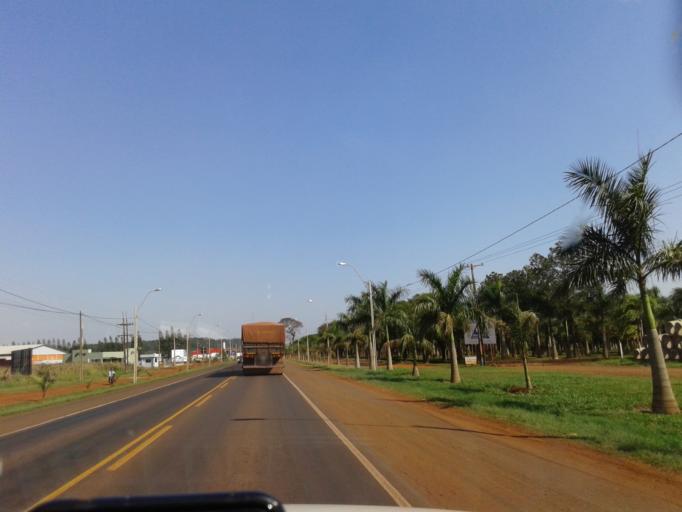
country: PY
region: Alto Parana
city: Santa Rita
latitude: -25.7543
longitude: -55.0589
